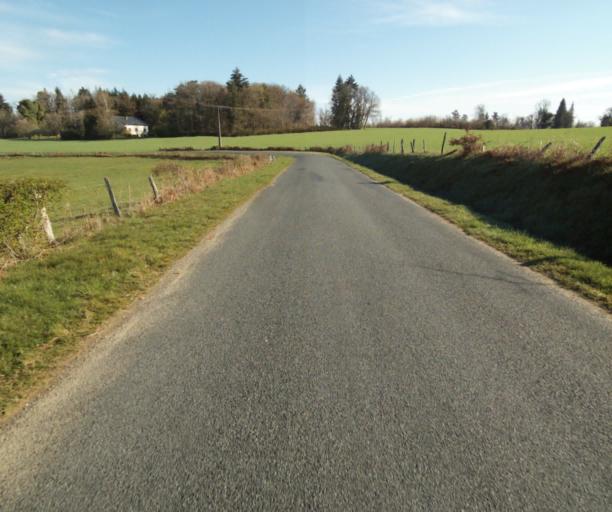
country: FR
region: Limousin
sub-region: Departement de la Correze
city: Correze
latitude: 45.3001
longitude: 1.8703
